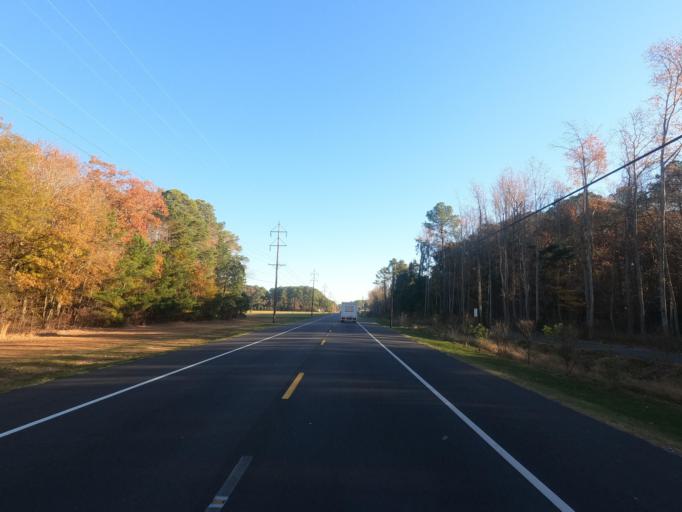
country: US
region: Maryland
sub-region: Somerset County
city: Crisfield
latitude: 37.9975
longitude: -75.8344
